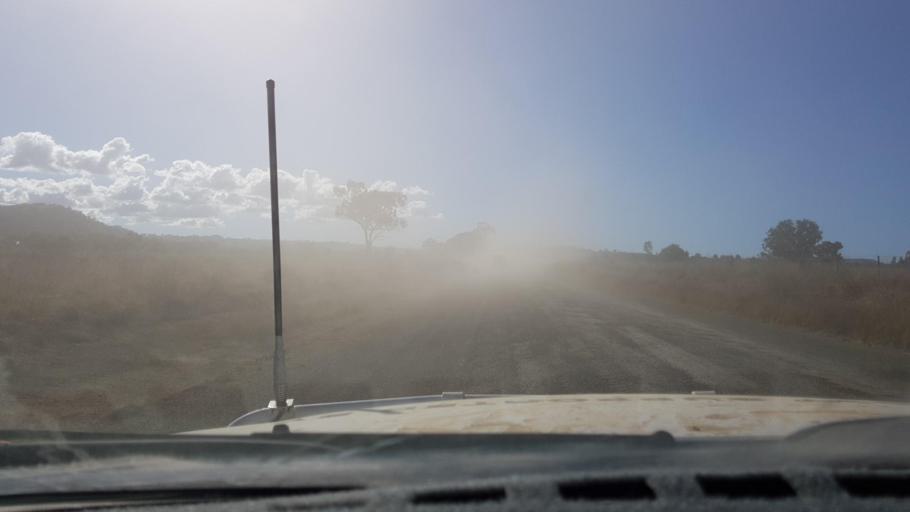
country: AU
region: New South Wales
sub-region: Narrabri
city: Blair Athol
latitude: -30.6712
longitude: 150.4537
